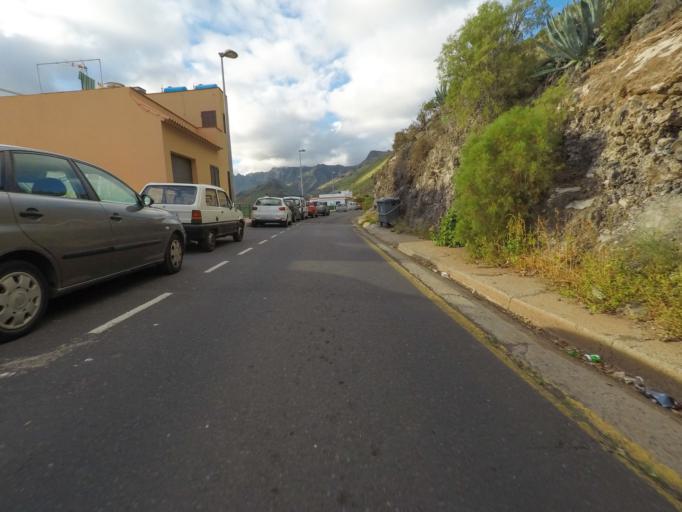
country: ES
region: Canary Islands
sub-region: Provincia de Santa Cruz de Tenerife
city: San Sebastian de la Gomera
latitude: 28.0954
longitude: -17.1129
